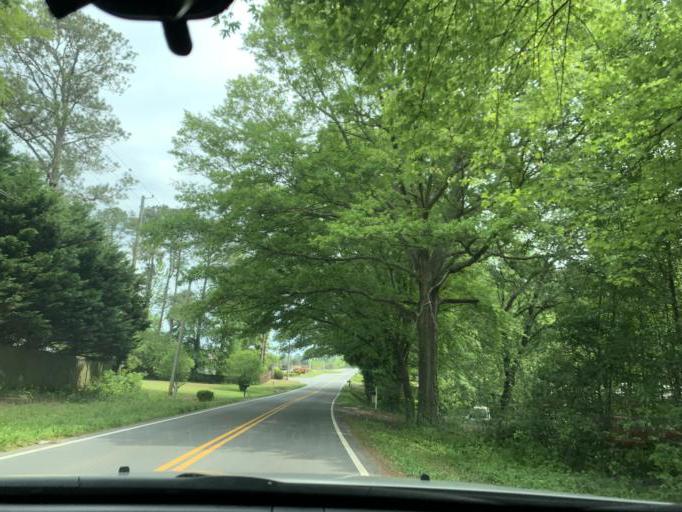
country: US
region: Georgia
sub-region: Fulton County
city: Milton
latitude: 34.1398
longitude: -84.2065
